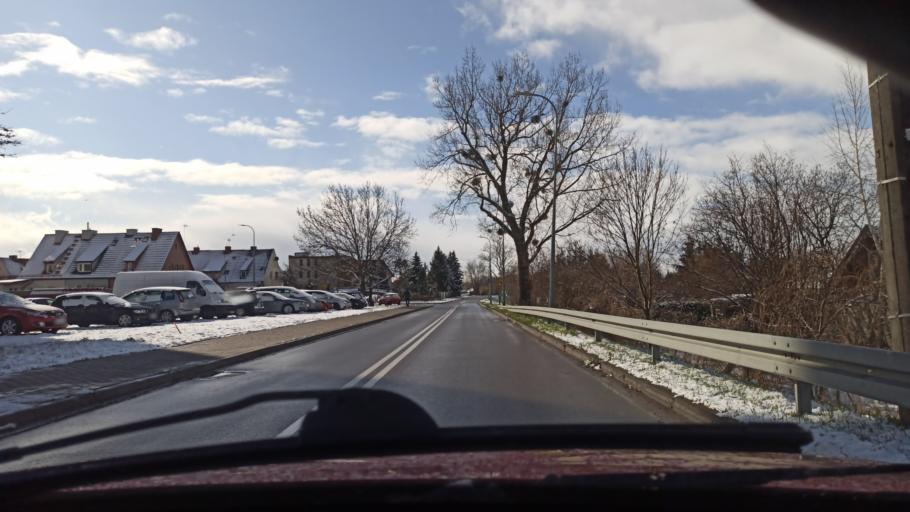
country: PL
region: Warmian-Masurian Voivodeship
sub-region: Powiat elblaski
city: Elblag
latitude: 54.1466
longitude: 19.4035
